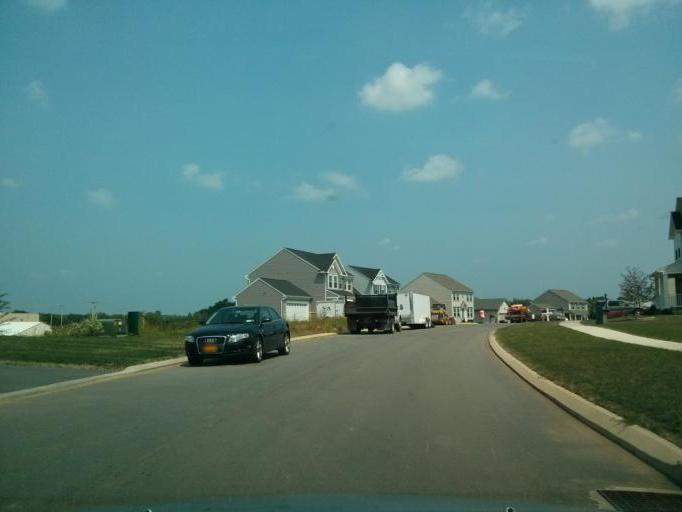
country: US
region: Pennsylvania
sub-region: Centre County
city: State College
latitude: 40.7713
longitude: -77.8843
